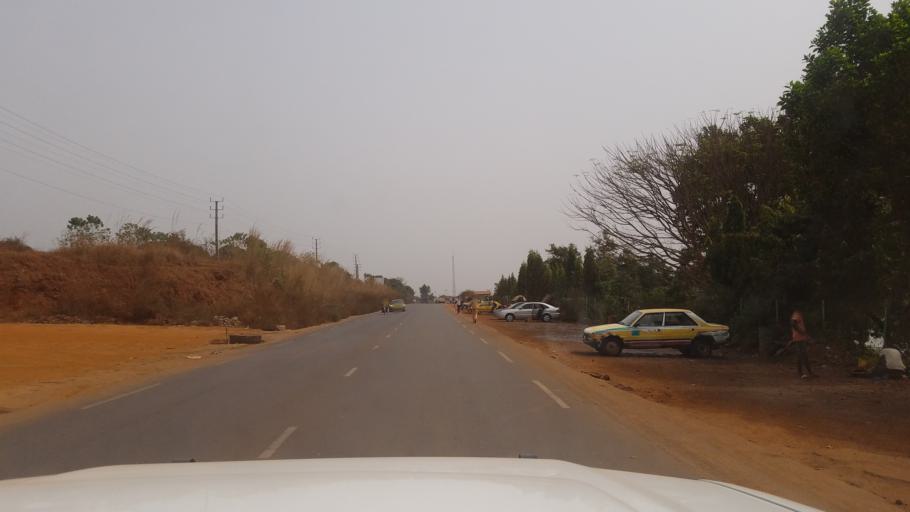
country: GN
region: Kindia
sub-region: Prefecture de Dubreka
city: Dubreka
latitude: 9.6756
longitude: -13.5833
